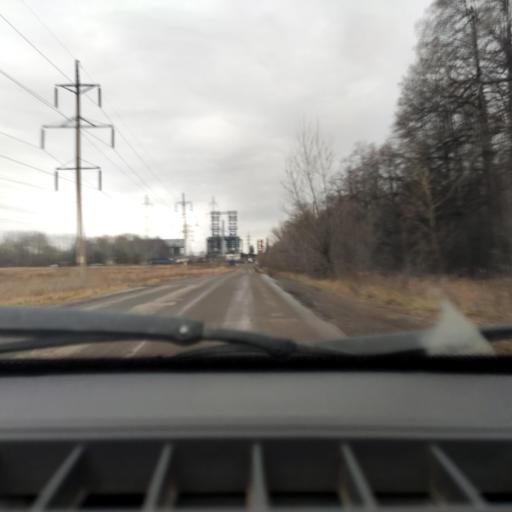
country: RU
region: Bashkortostan
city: Blagoveshchensk
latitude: 54.9389
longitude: 56.0845
